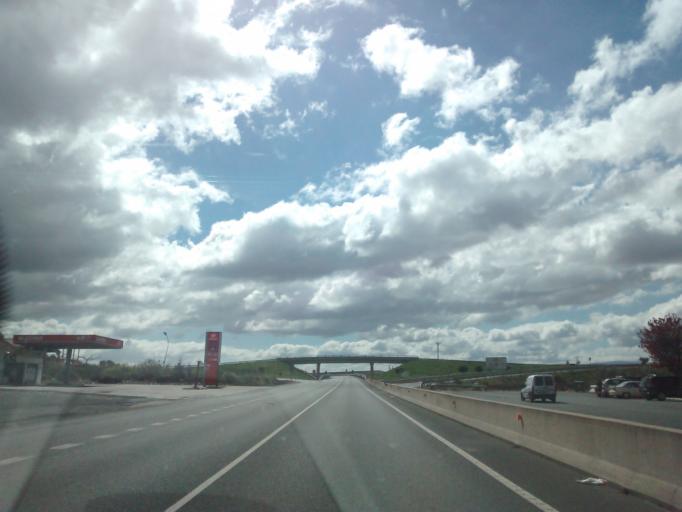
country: ES
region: La Rioja
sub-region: Provincia de La Rioja
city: San Asensio
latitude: 42.5144
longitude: -2.7415
